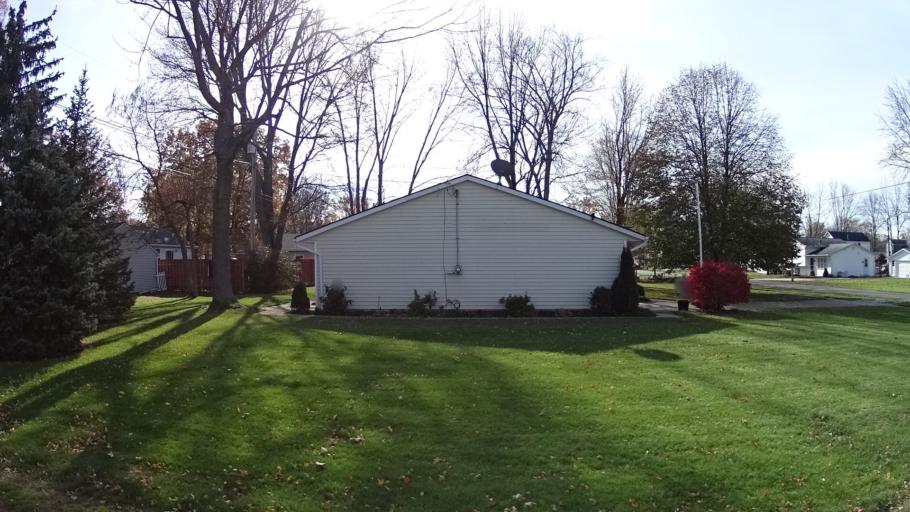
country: US
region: Ohio
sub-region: Lorain County
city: Sheffield Lake
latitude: 41.4875
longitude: -82.1002
